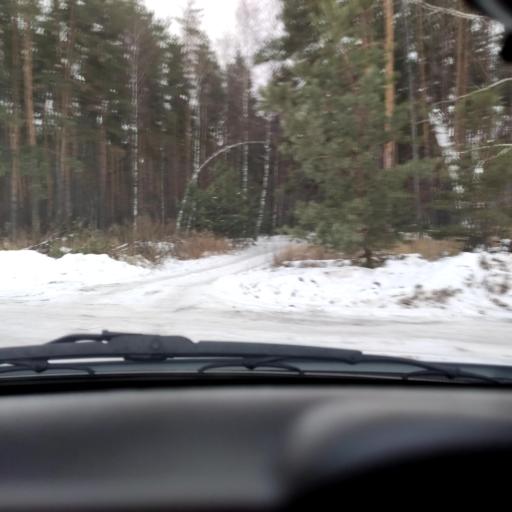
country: RU
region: Voronezj
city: Ramon'
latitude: 51.8838
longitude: 39.2608
